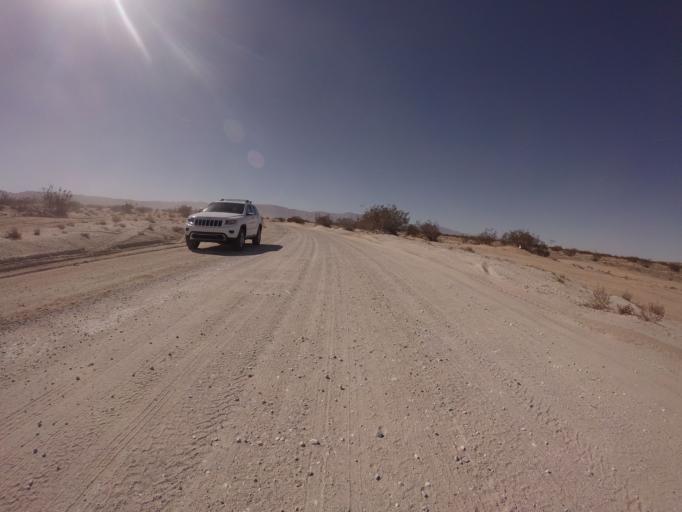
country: US
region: California
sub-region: San Bernardino County
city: Yucca Valley
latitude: 34.3873
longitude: -116.5364
